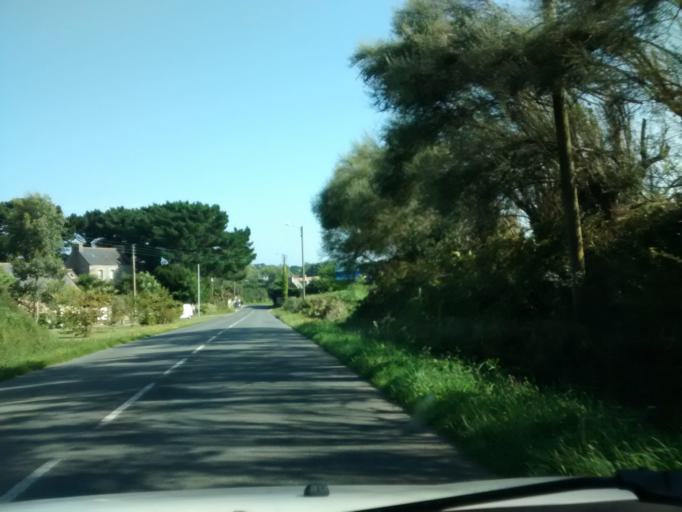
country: FR
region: Brittany
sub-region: Departement des Cotes-d'Armor
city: Pleubian
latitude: 48.8496
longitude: -3.1296
